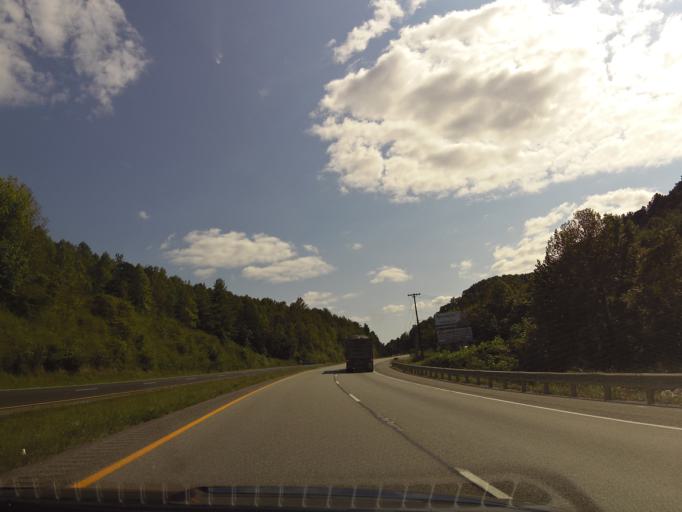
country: US
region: Kentucky
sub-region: Bell County
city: Pineville
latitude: 36.7269
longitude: -83.6902
